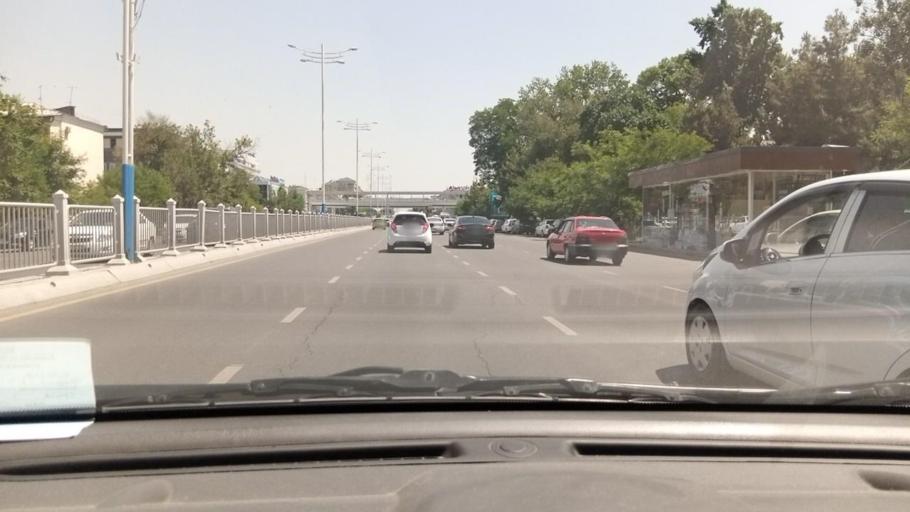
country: UZ
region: Toshkent Shahri
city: Tashkent
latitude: 41.2938
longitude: 69.2205
